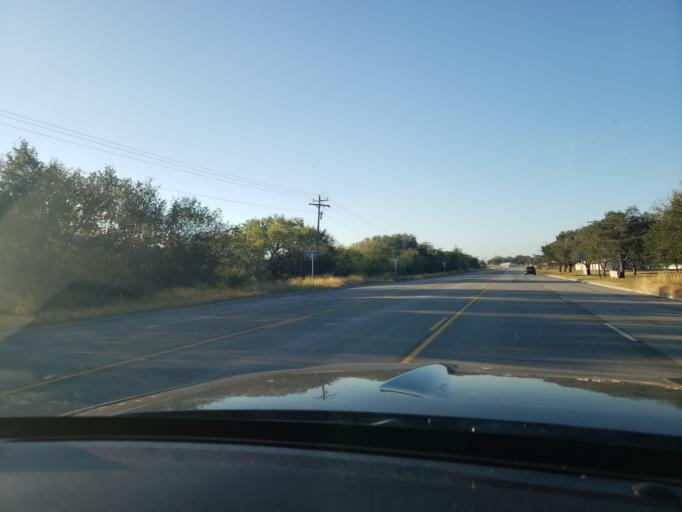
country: US
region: Texas
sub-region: Bee County
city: Beeville
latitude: 28.4252
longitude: -97.7167
